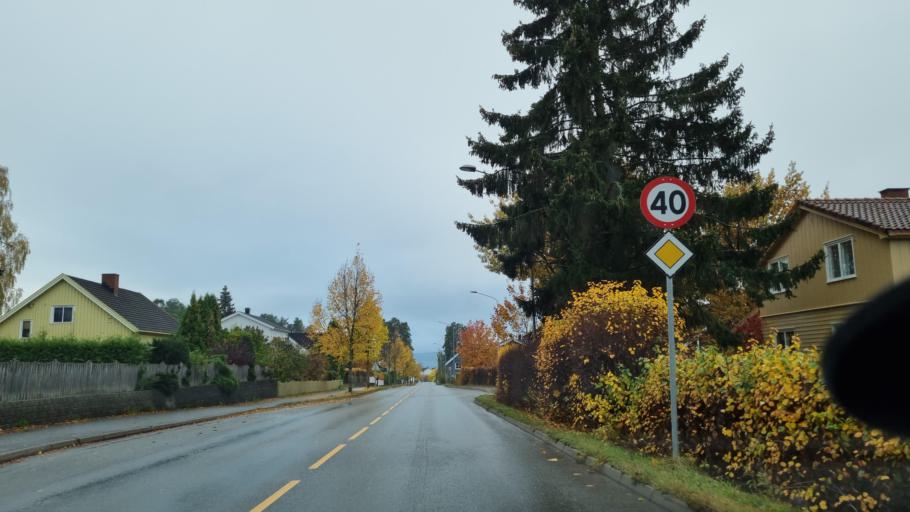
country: NO
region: Hedmark
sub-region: Hamar
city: Hamar
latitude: 60.8020
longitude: 11.0631
